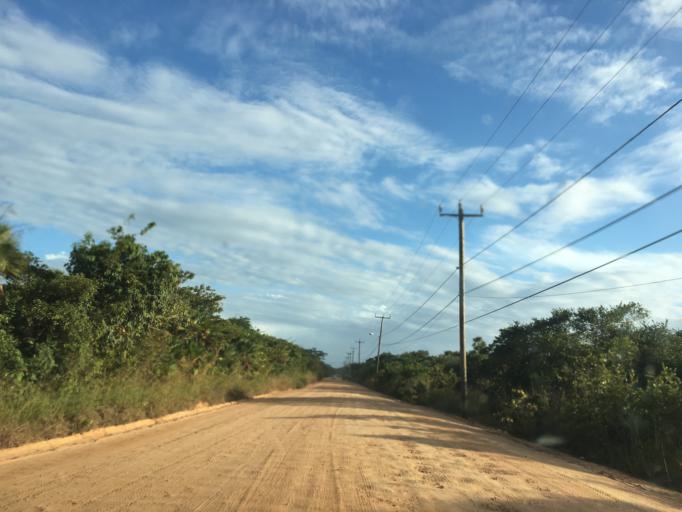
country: BZ
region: Stann Creek
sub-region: Dangriga
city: Dangriga
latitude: 16.8454
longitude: -88.2774
